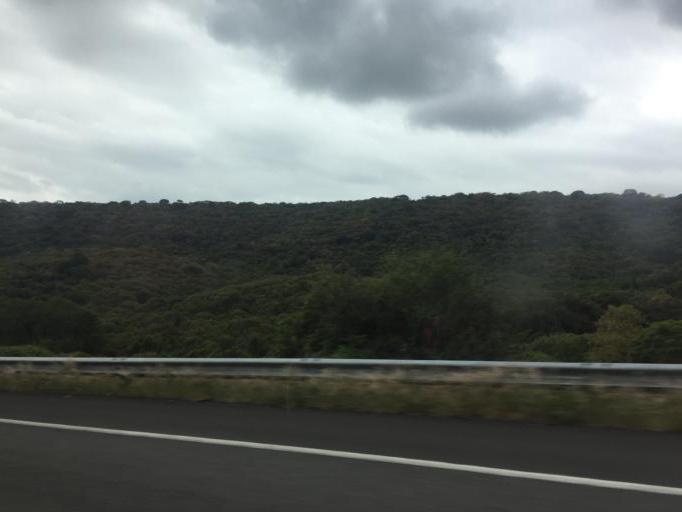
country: MX
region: Jalisco
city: Ocotlan
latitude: 20.4212
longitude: -102.7650
